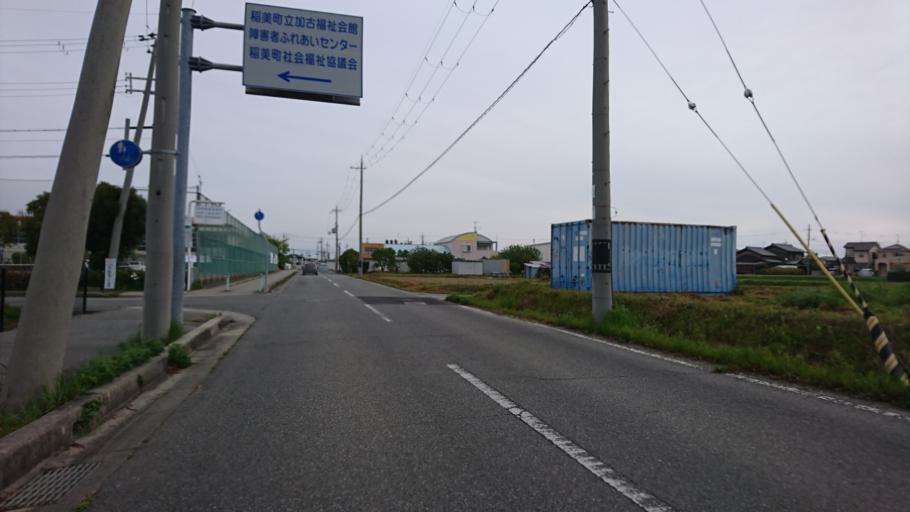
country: JP
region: Hyogo
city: Kakogawacho-honmachi
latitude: 34.7610
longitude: 134.9081
